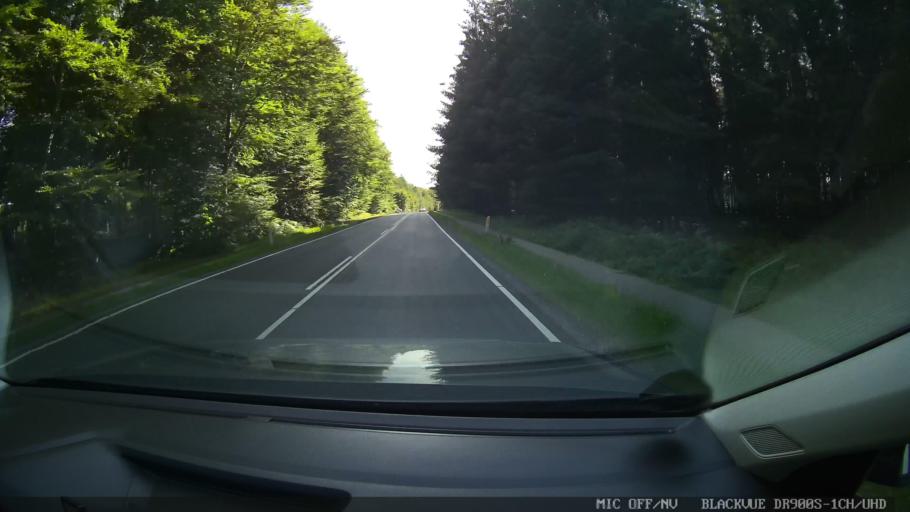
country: DK
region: North Denmark
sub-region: Mariagerfjord Kommune
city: Arden
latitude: 56.7819
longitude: 9.7487
